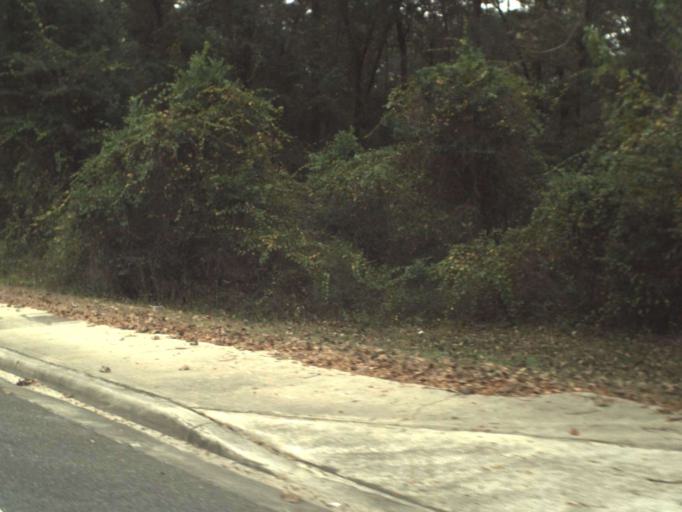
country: US
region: Florida
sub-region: Leon County
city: Tallahassee
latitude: 30.3688
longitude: -84.2960
